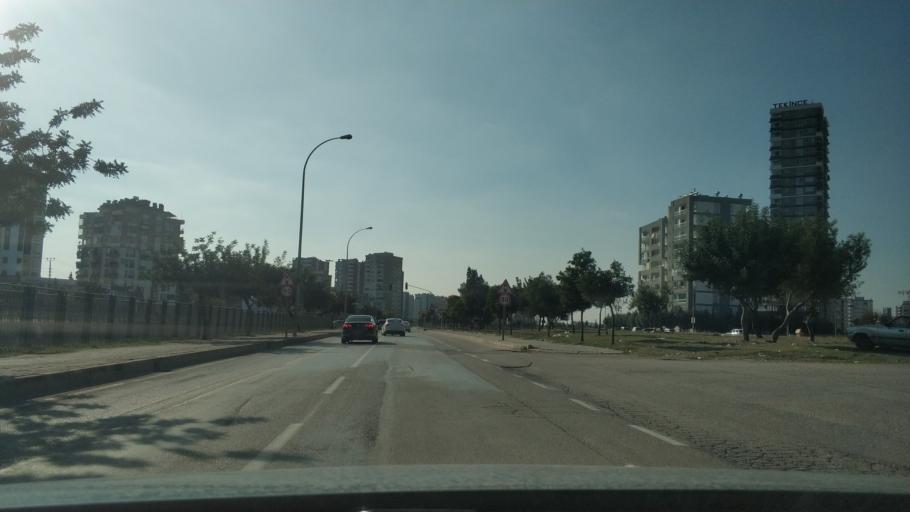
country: TR
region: Adana
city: Seyhan
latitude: 37.0107
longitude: 35.2738
